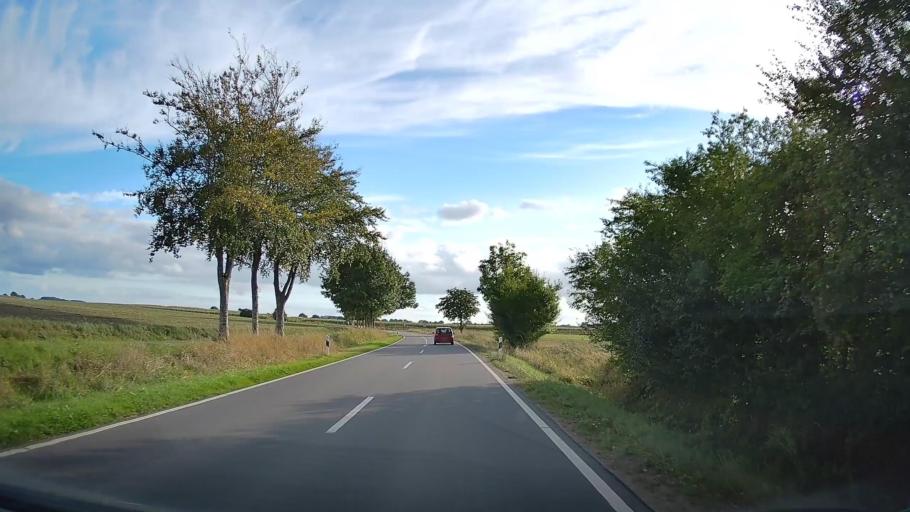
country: DE
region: Schleswig-Holstein
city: Pommerby
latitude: 54.7593
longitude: 9.9437
